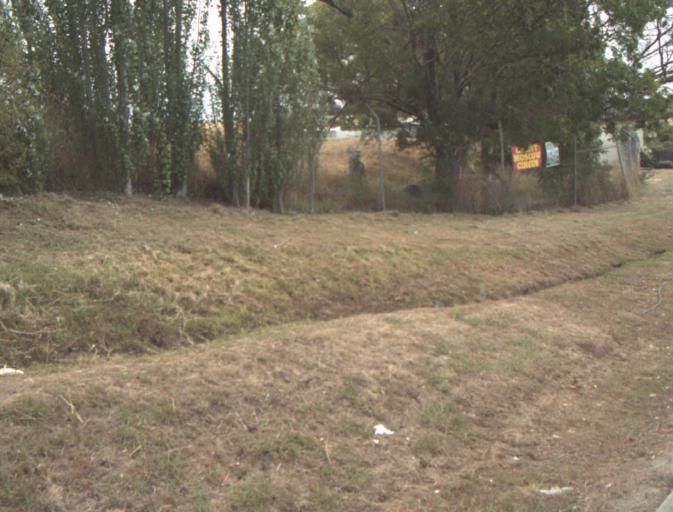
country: AU
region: Tasmania
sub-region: Launceston
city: Newstead
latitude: -41.4377
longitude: 147.1768
